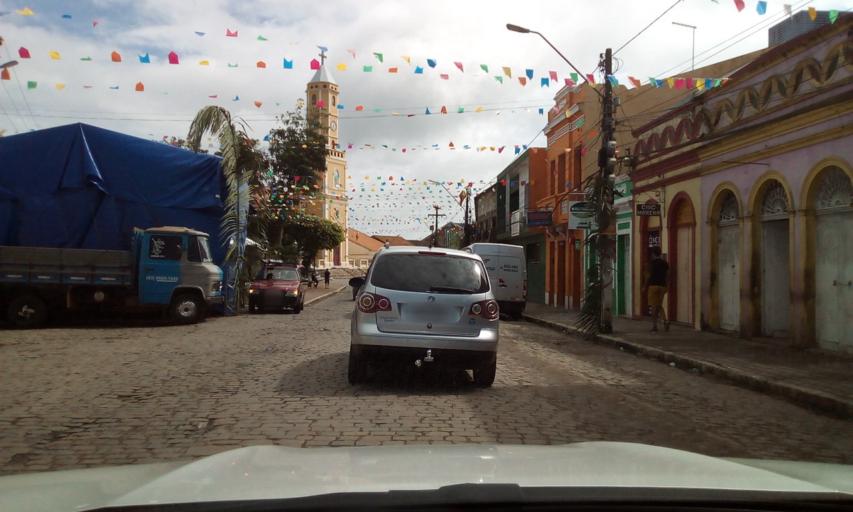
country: BR
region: Paraiba
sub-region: Areia
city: Areia
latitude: -6.9686
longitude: -35.7033
